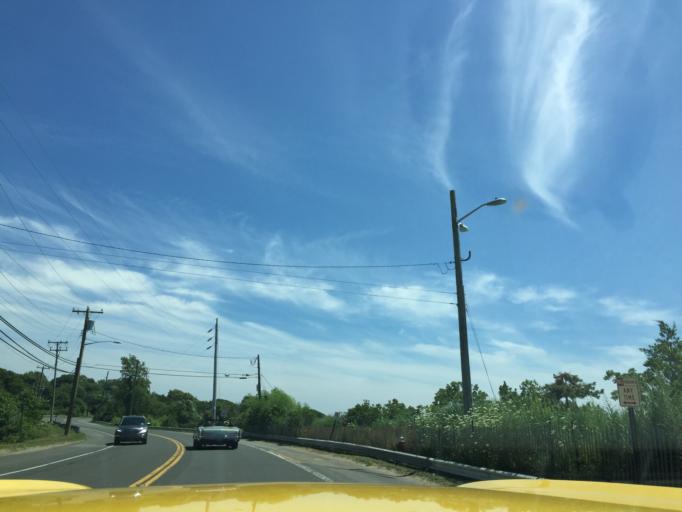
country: US
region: New York
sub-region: Suffolk County
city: Montauk
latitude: 41.0443
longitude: -71.9503
